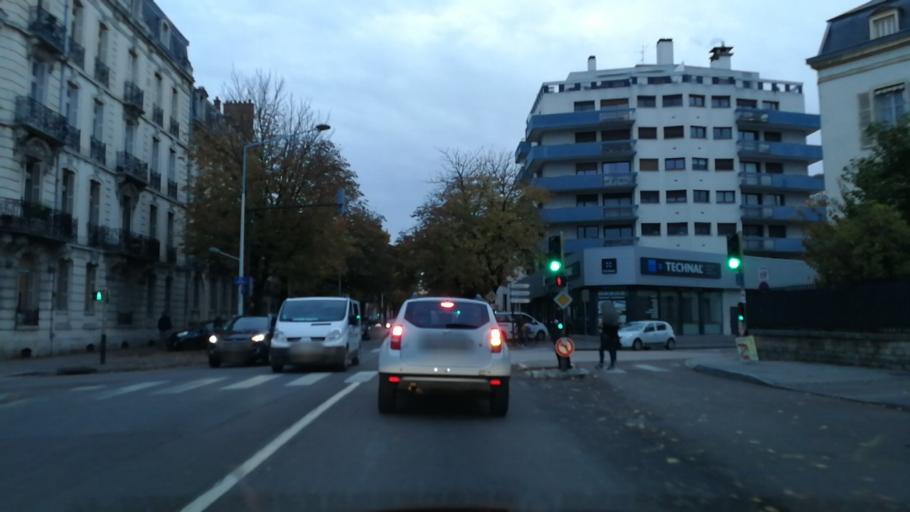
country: FR
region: Bourgogne
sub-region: Departement de la Cote-d'Or
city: Dijon
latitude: 47.3193
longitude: 5.0482
